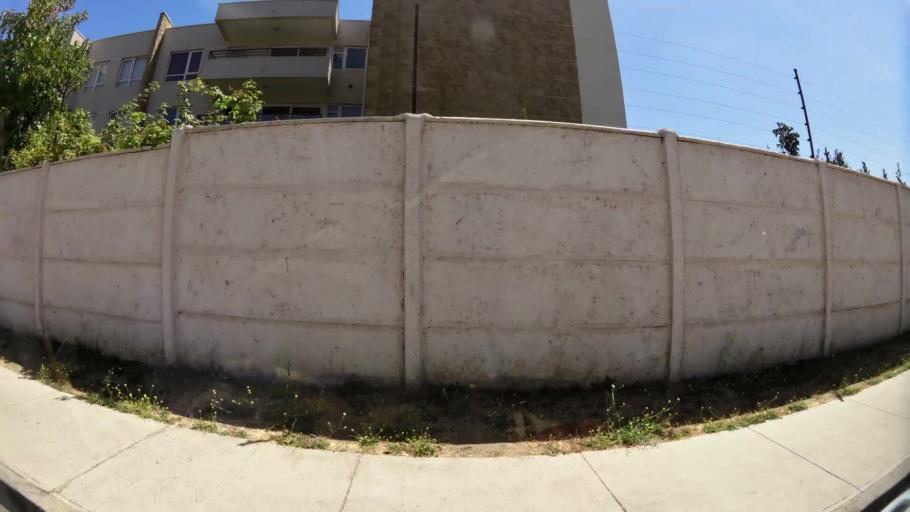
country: CL
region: Maule
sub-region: Provincia de Talca
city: Talca
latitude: -35.4323
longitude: -71.6229
